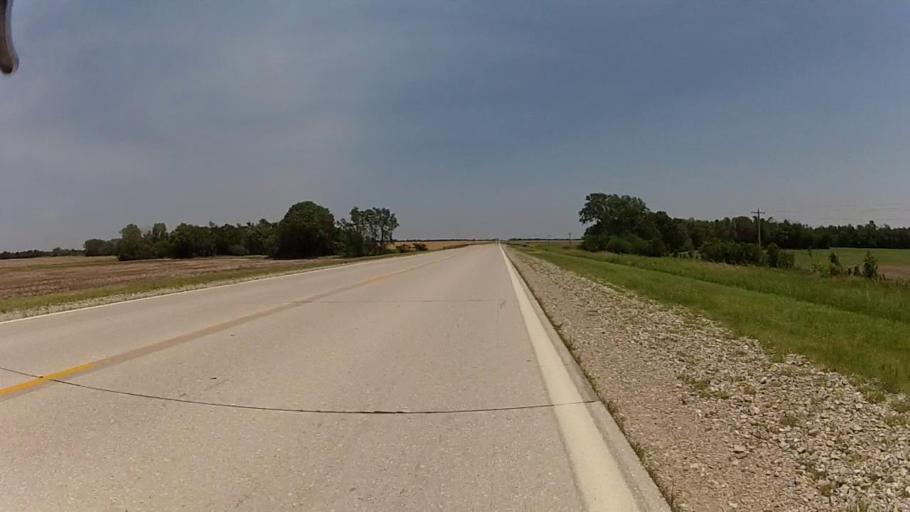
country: US
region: Kansas
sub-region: Sumner County
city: Wellington
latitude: 37.0574
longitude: -97.2884
